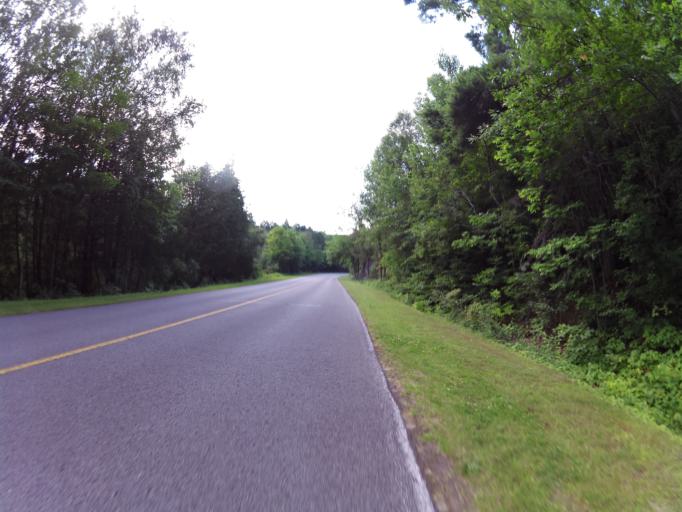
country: CA
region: Quebec
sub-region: Outaouais
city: Gatineau
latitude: 45.4573
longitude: -75.7885
